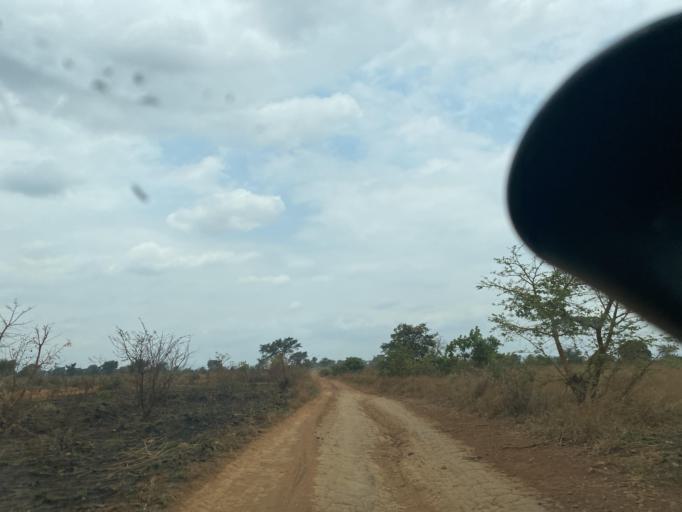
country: ZM
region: Lusaka
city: Chongwe
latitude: -15.4955
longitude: 28.7992
